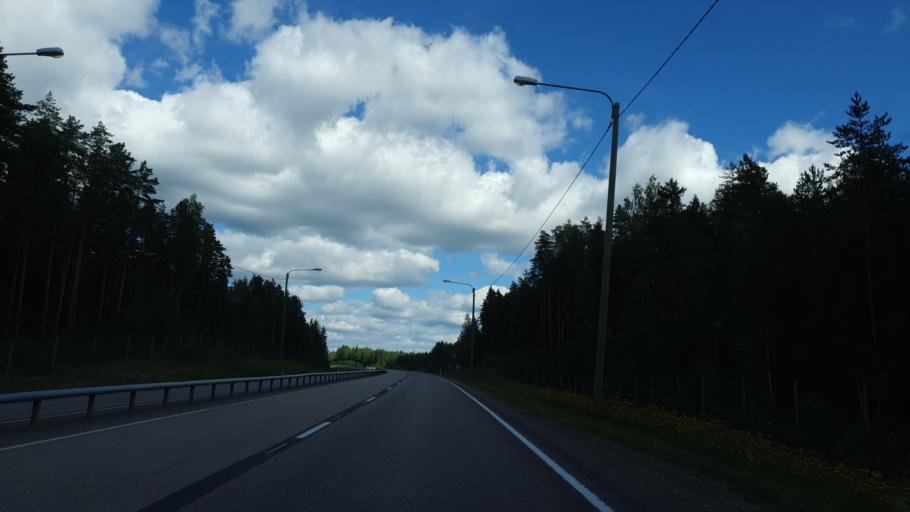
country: FI
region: Central Finland
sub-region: Jaemsae
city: Jaemsae
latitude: 61.8099
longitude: 24.9978
